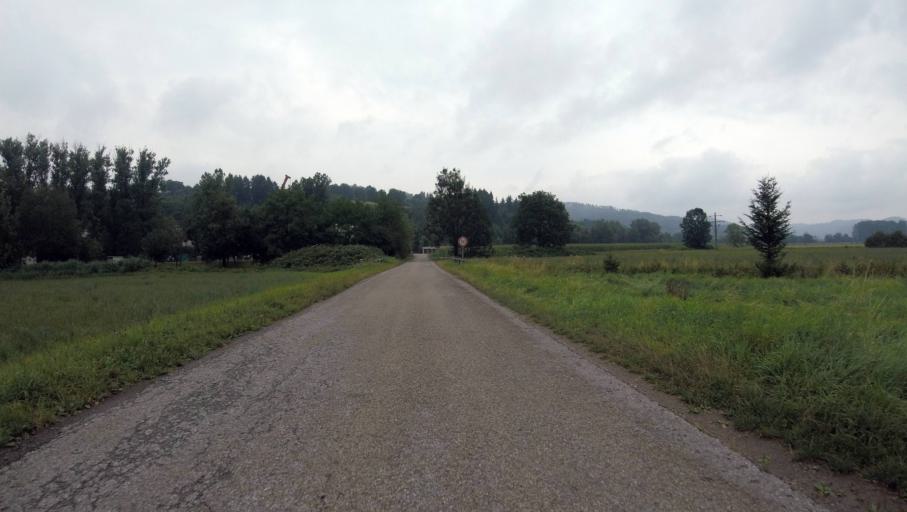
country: DE
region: Baden-Wuerttemberg
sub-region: Regierungsbezirk Stuttgart
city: Oppenweiler
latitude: 48.9907
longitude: 9.4692
